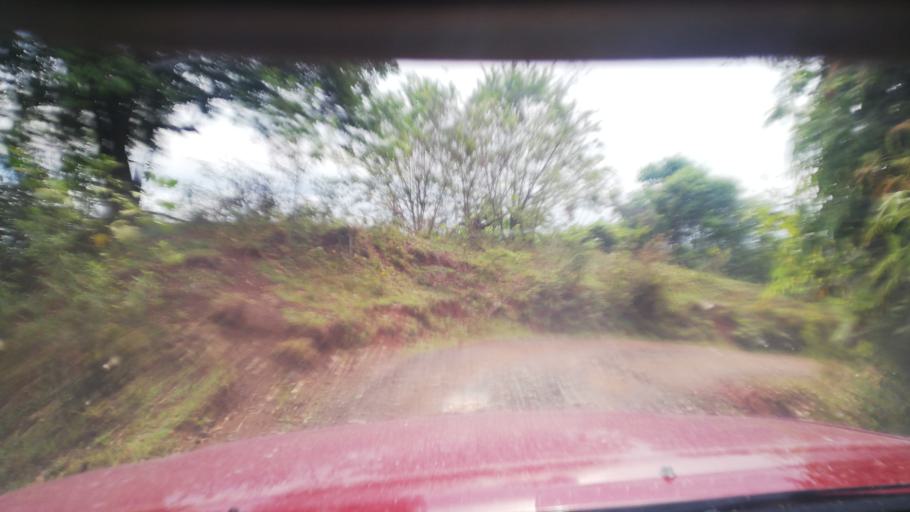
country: CO
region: Risaralda
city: La Virginia
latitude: 4.8770
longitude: -75.9425
